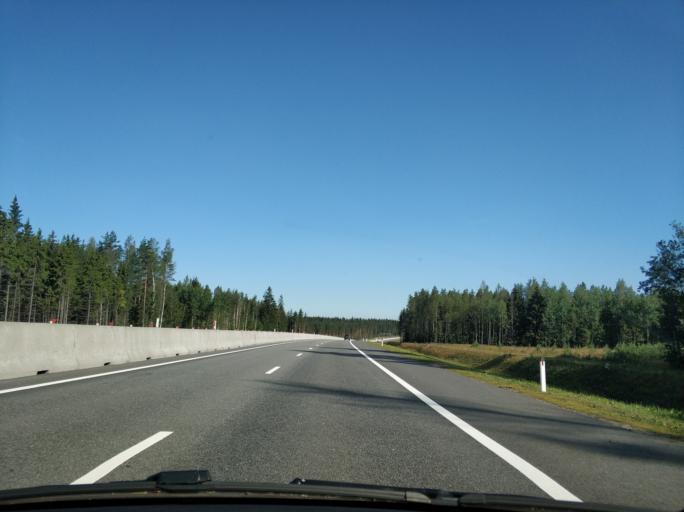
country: RU
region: Leningrad
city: Sosnovo
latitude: 60.5258
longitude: 30.1672
